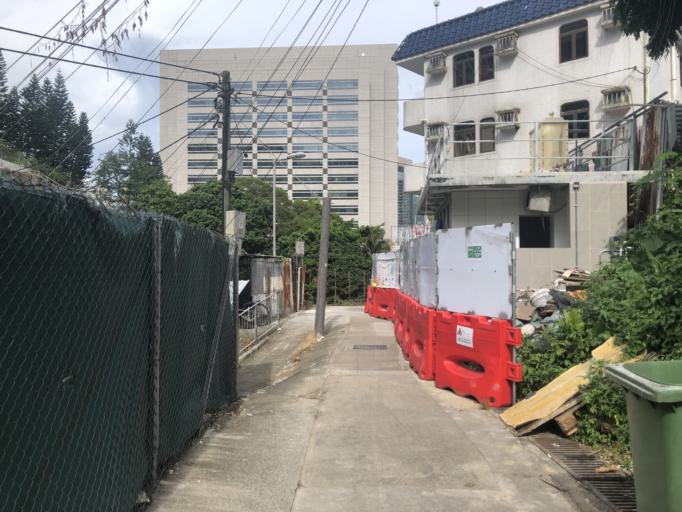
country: HK
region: Sha Tin
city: Sha Tin
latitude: 22.3856
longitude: 114.1853
